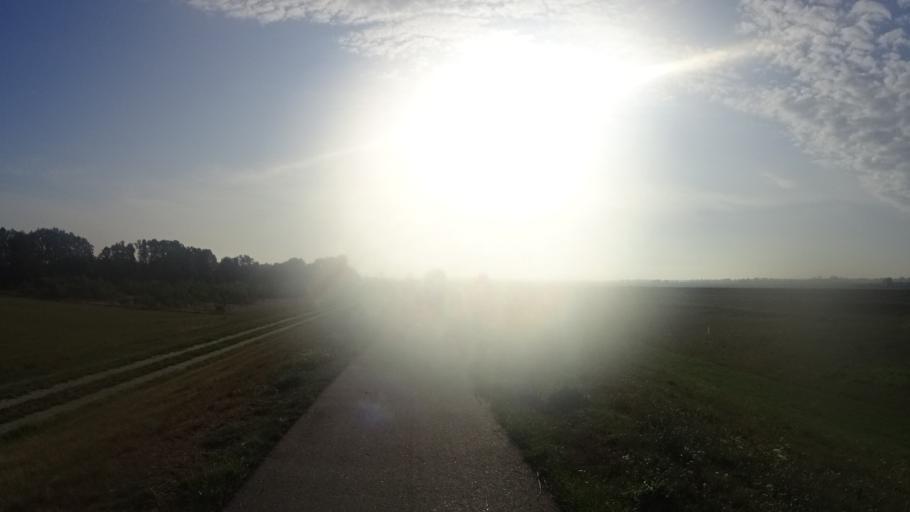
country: DE
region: Brandenburg
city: Lanz
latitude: 53.0576
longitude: 11.5434
